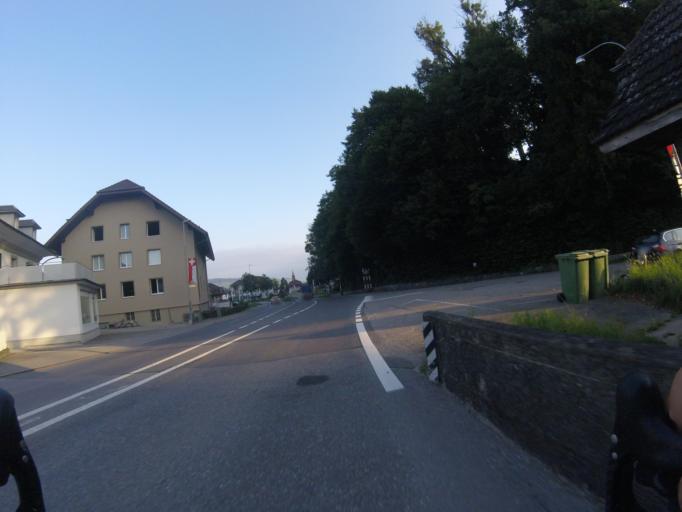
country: CH
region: Bern
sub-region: Thun District
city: Uttigen
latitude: 46.8192
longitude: 7.5875
